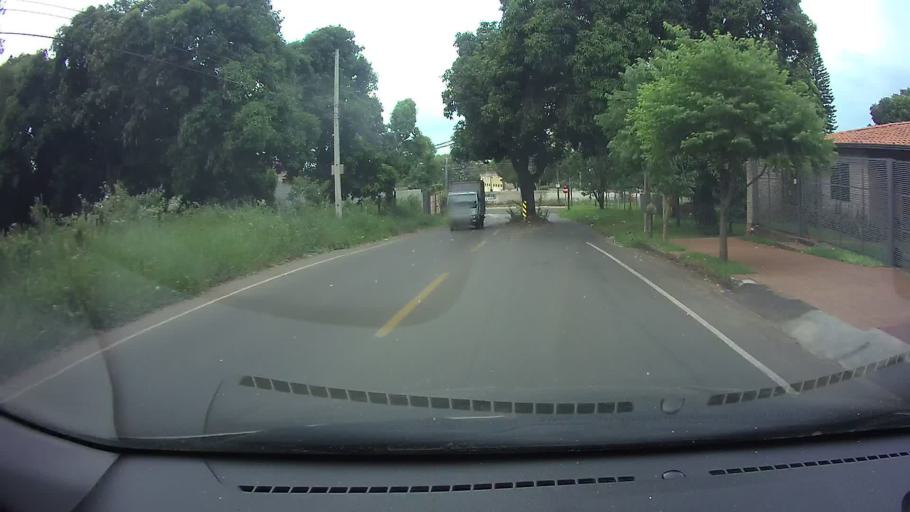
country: PY
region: Central
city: San Lorenzo
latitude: -25.2716
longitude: -57.4767
